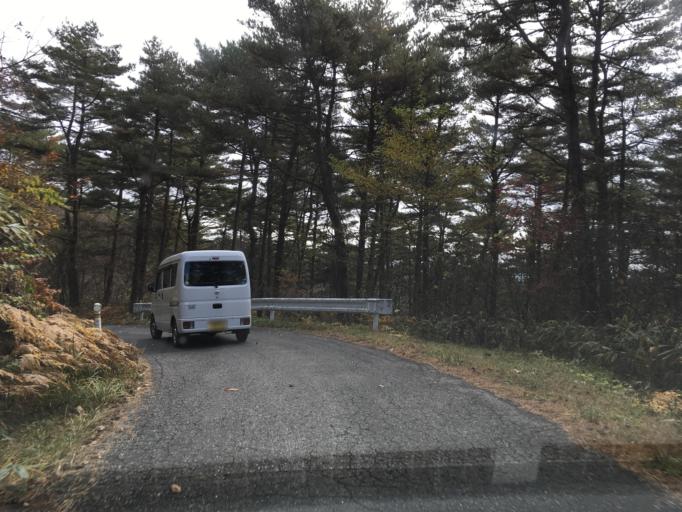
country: JP
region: Iwate
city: Mizusawa
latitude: 39.1290
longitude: 141.3081
